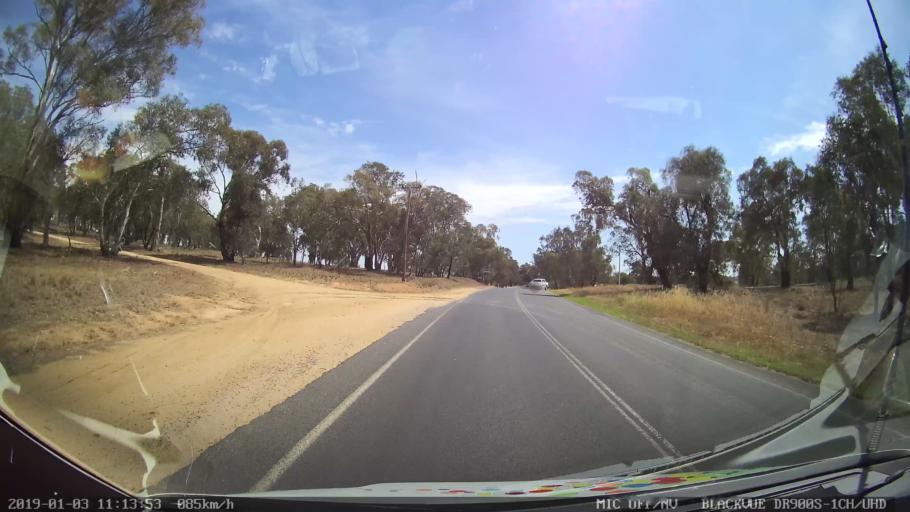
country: AU
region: New South Wales
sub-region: Young
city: Young
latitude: -34.1830
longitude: 148.2598
